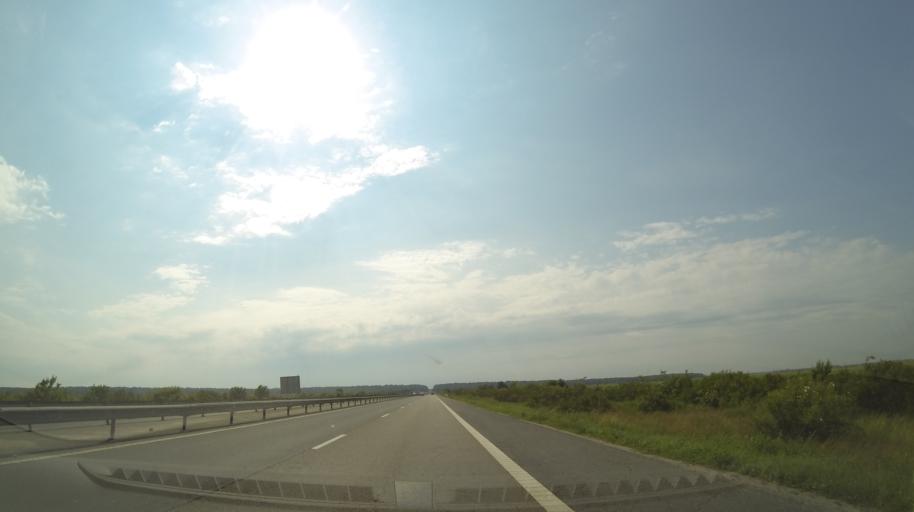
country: RO
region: Giurgiu
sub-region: Comuna Vanatorii Mici
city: Vanatorii Mici
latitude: 44.5200
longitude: 25.5522
